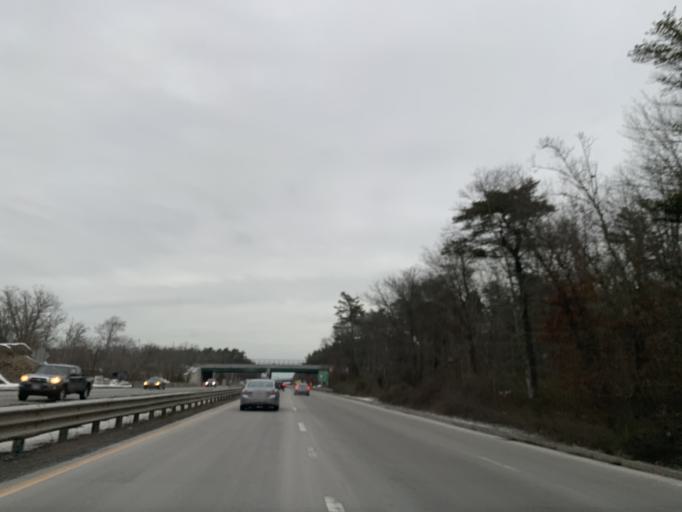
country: US
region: Massachusetts
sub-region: Bristol County
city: Raynham Center
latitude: 41.9044
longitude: -71.0435
